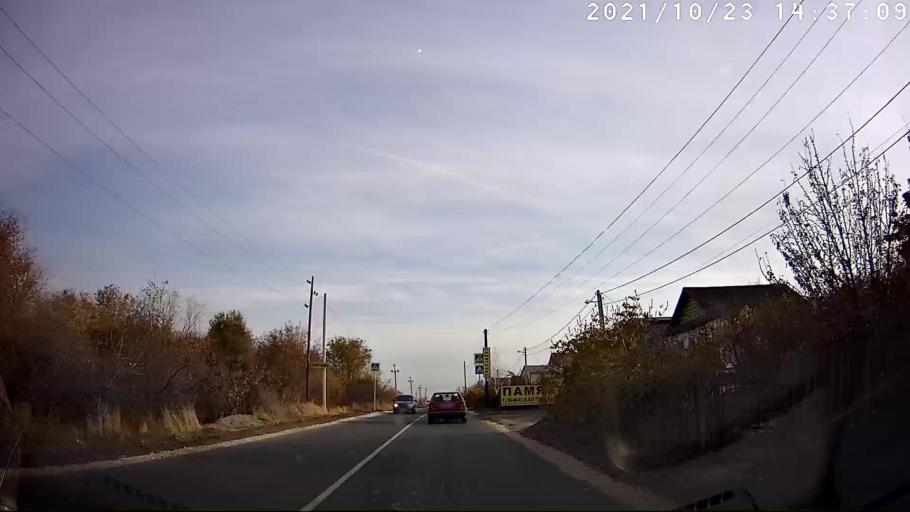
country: RU
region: Volgograd
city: Krasnoslobodsk
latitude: 48.4990
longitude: 44.5469
